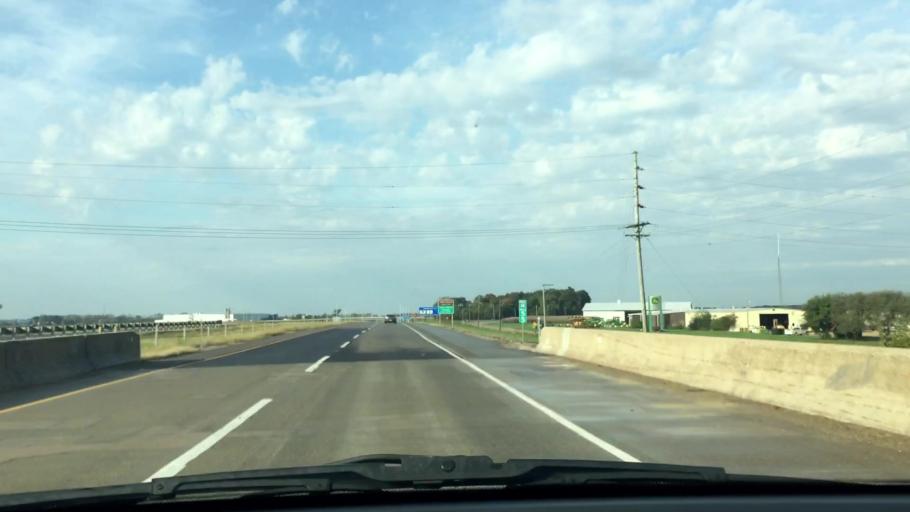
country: US
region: Illinois
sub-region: Lee County
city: Dixon
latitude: 41.8243
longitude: -89.4534
